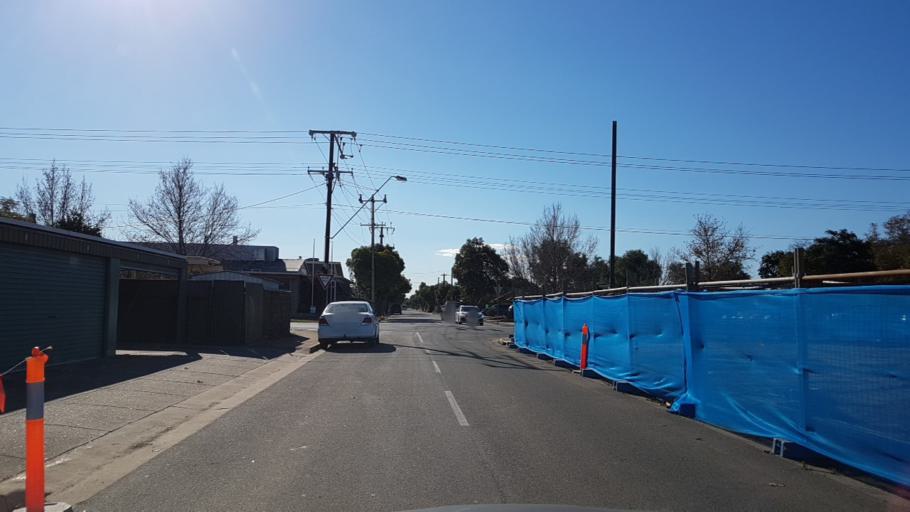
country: AU
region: South Australia
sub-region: City of West Torrens
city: Plympton
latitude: -34.9606
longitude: 138.5457
